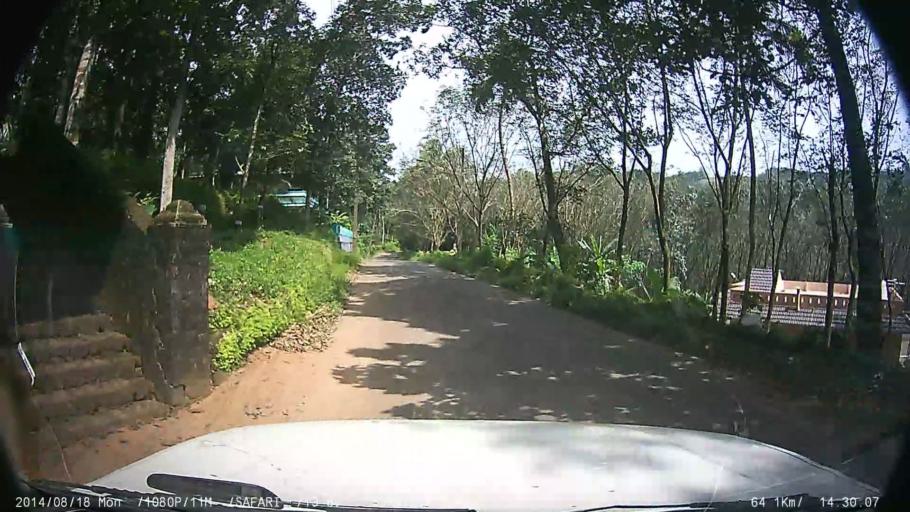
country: IN
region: Kerala
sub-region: Ernakulam
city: Piravam
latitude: 9.7896
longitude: 76.5495
